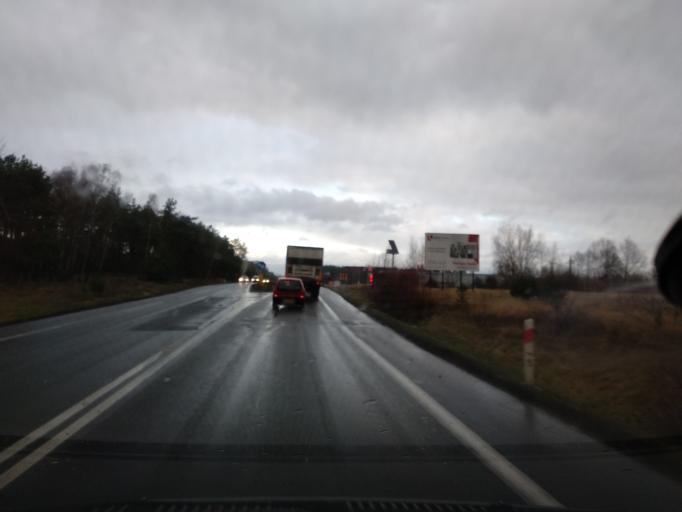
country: PL
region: Greater Poland Voivodeship
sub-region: Powiat koninski
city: Stare Miasto
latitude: 52.1687
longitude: 18.2112
